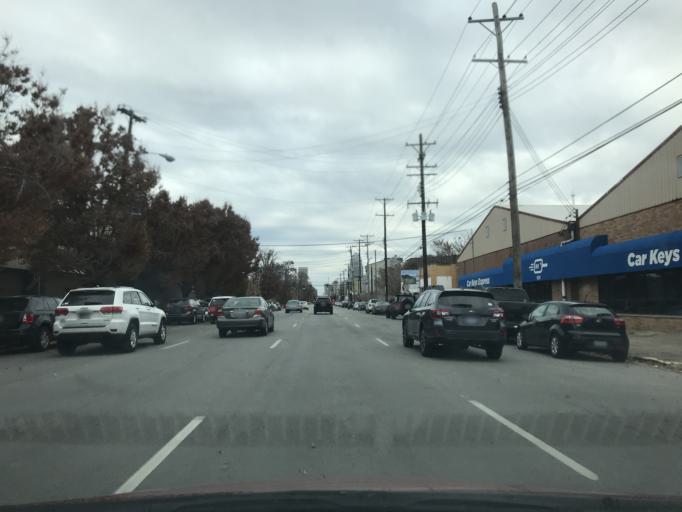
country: US
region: Kentucky
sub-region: Jefferson County
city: Louisville
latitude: 38.2517
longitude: -85.7368
